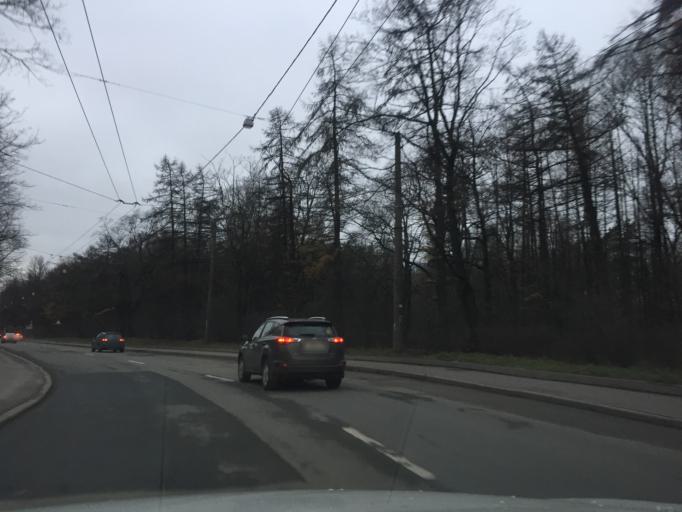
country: RU
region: Leningrad
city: Sampsonievskiy
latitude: 59.9934
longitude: 30.3516
